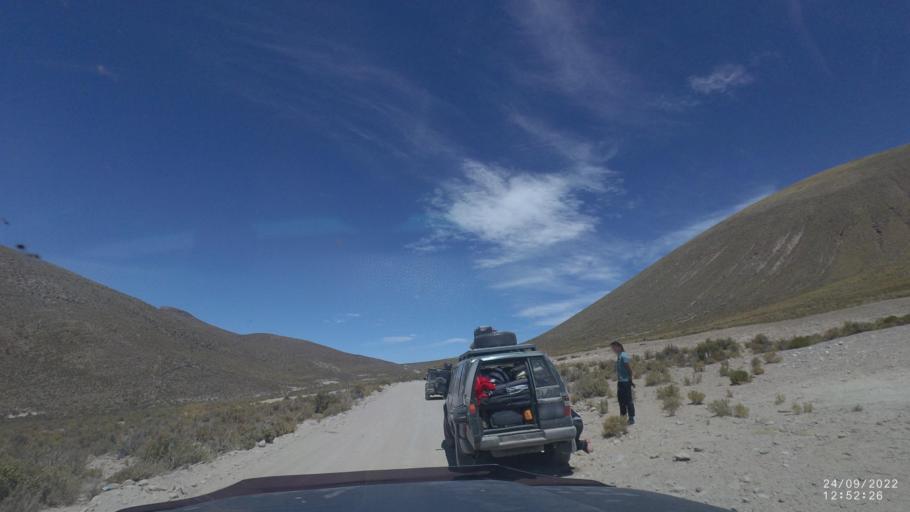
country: BO
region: Potosi
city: Colchani
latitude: -19.8121
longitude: -67.5673
